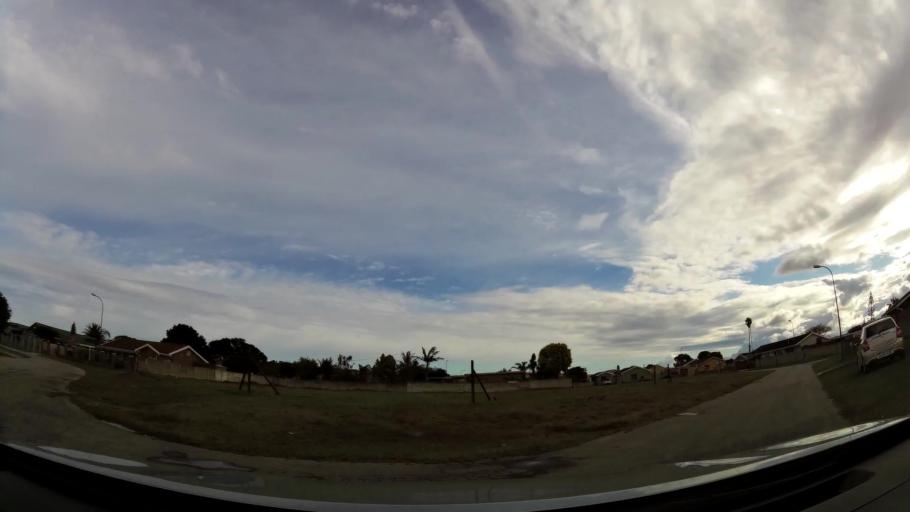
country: ZA
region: Eastern Cape
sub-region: Nelson Mandela Bay Metropolitan Municipality
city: Port Elizabeth
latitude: -33.9383
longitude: 25.4656
